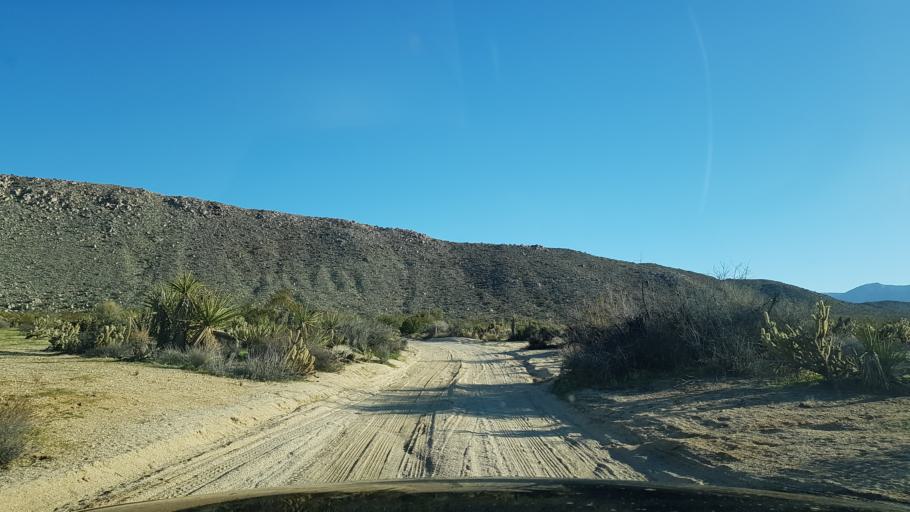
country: US
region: California
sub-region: San Diego County
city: Julian
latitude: 33.0077
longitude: -116.3911
